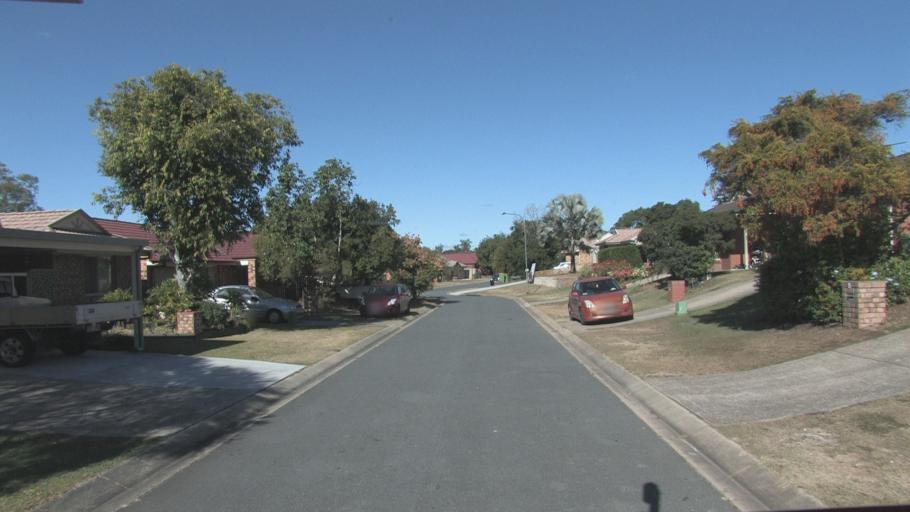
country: AU
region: Queensland
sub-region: Logan
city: Park Ridge South
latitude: -27.6740
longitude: 153.0202
